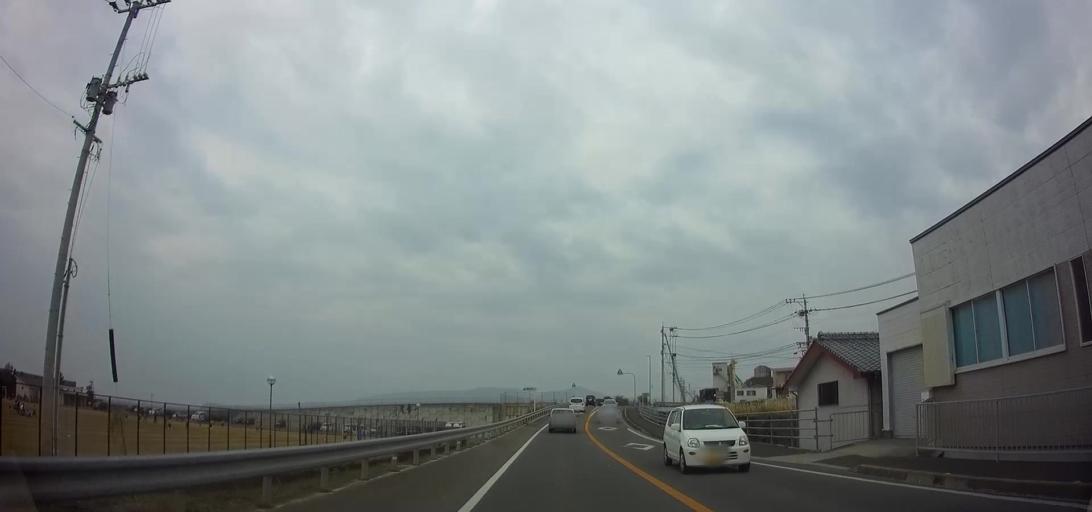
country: JP
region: Nagasaki
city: Shimabara
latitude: 32.6532
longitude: 130.2844
